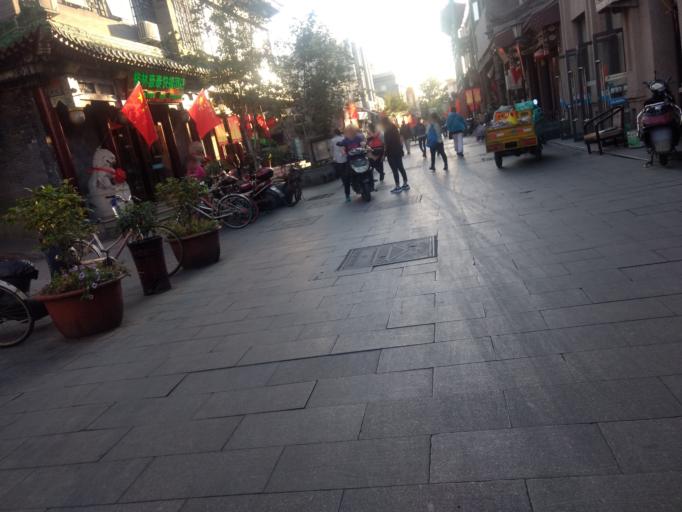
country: CN
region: Beijing
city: Beijing
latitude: 39.8936
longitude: 116.3866
